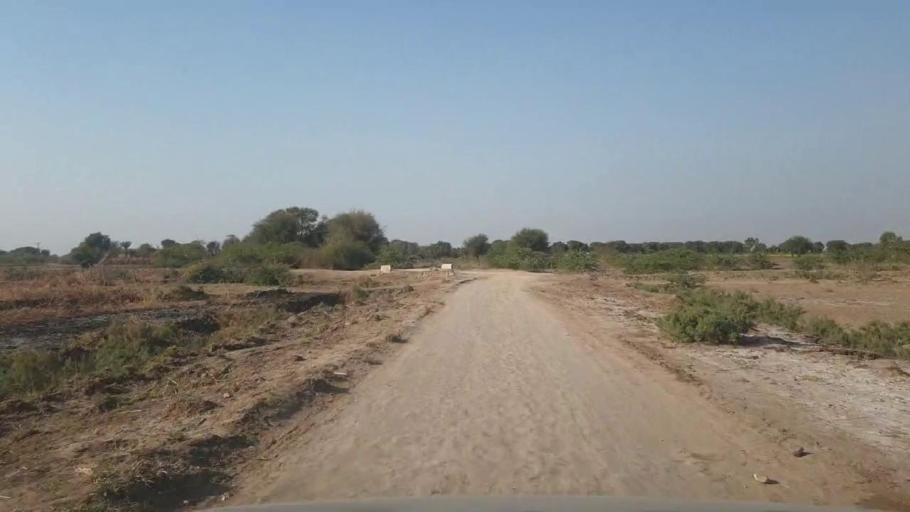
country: PK
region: Sindh
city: Chambar
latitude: 25.3011
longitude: 68.8624
